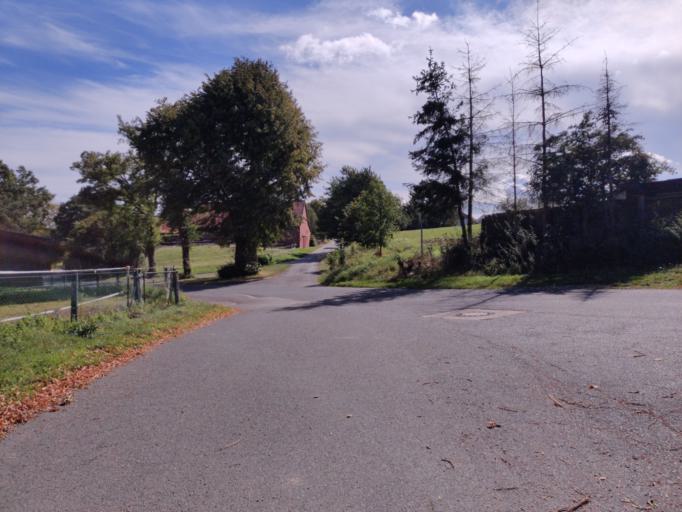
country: DE
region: Lower Saxony
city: Baddeckenstedt
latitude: 52.0829
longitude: 10.2276
